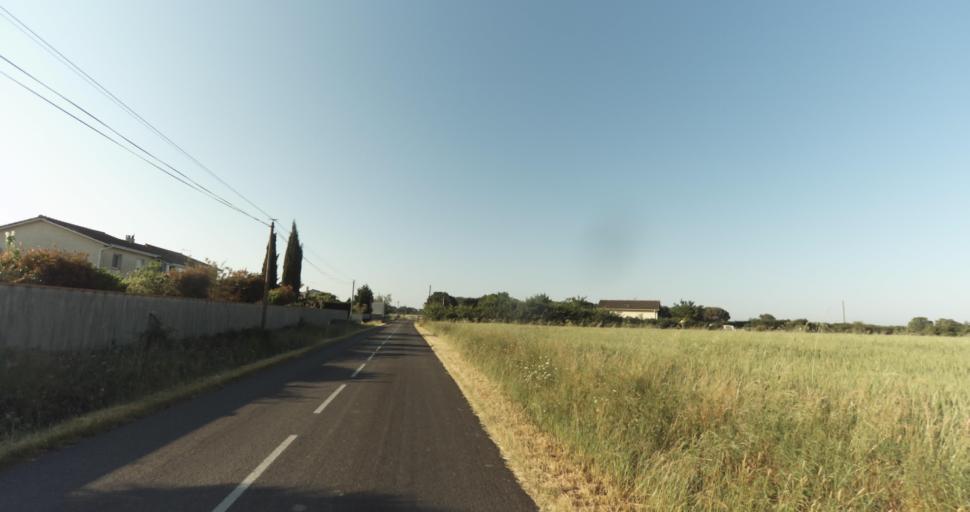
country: FR
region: Midi-Pyrenees
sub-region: Departement de la Haute-Garonne
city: Leguevin
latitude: 43.5892
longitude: 1.2364
